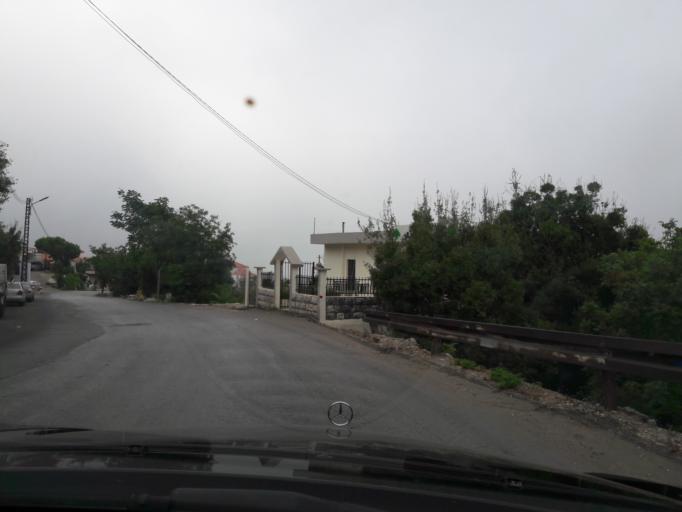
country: LB
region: Mont-Liban
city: Djounie
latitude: 33.9894
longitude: 35.6829
